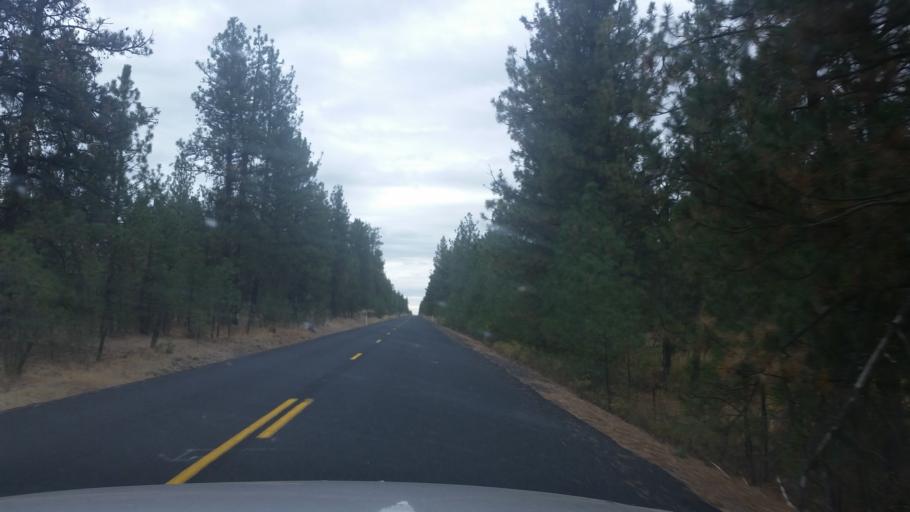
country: US
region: Washington
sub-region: Spokane County
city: Medical Lake
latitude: 47.4809
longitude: -117.7792
